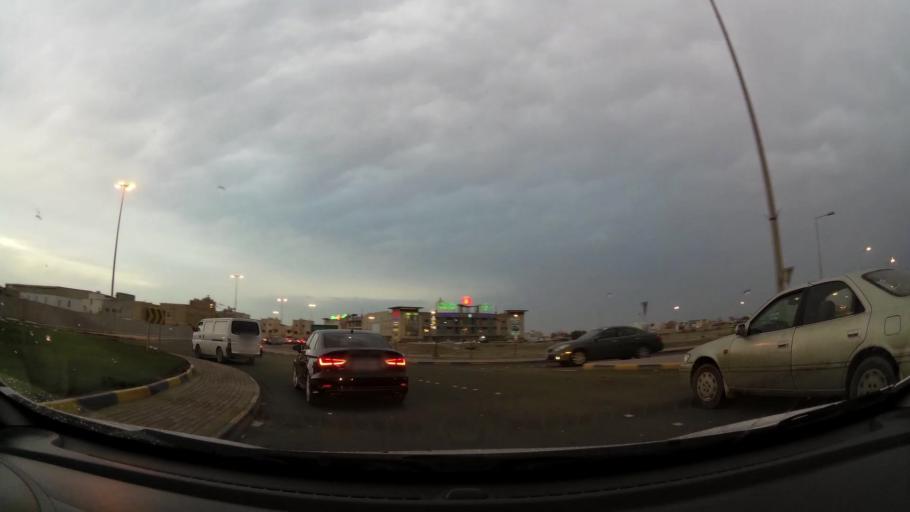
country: BH
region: Northern
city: Madinat `Isa
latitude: 26.1596
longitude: 50.5216
